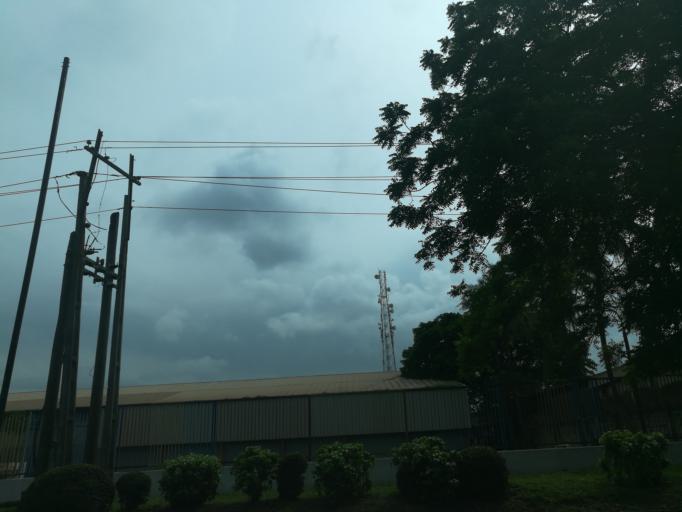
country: NG
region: Lagos
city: Ojota
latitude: 6.6045
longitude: 3.3717
